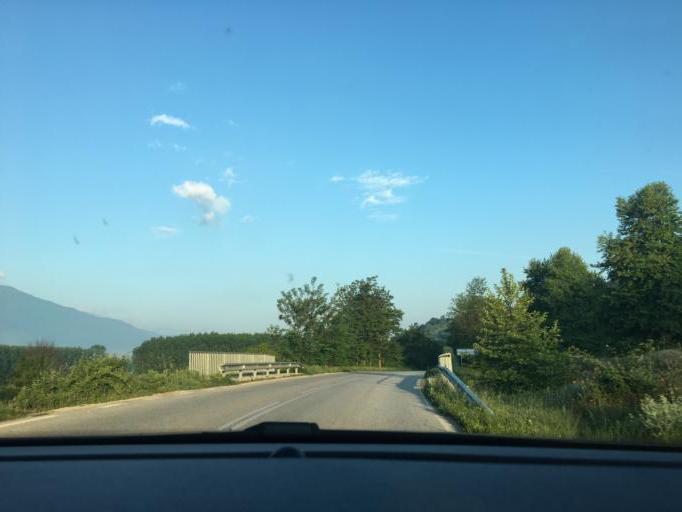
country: MK
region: Novo Selo
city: Novo Selo
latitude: 41.3980
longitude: 22.9872
